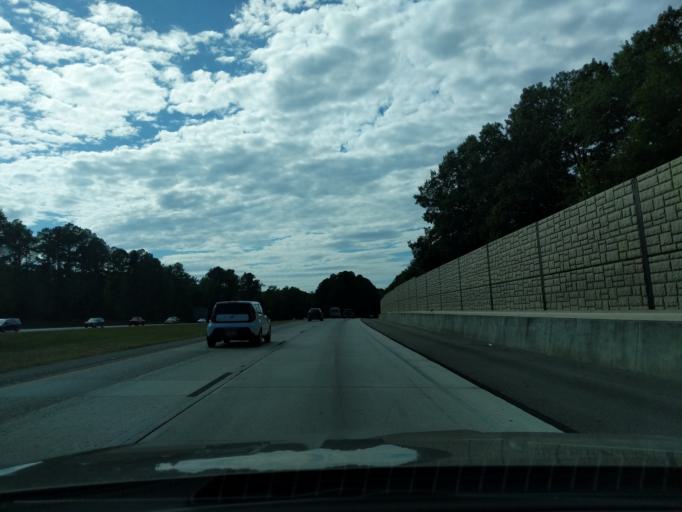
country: US
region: Georgia
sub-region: Columbia County
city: Evans
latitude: 33.4795
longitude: -82.1482
